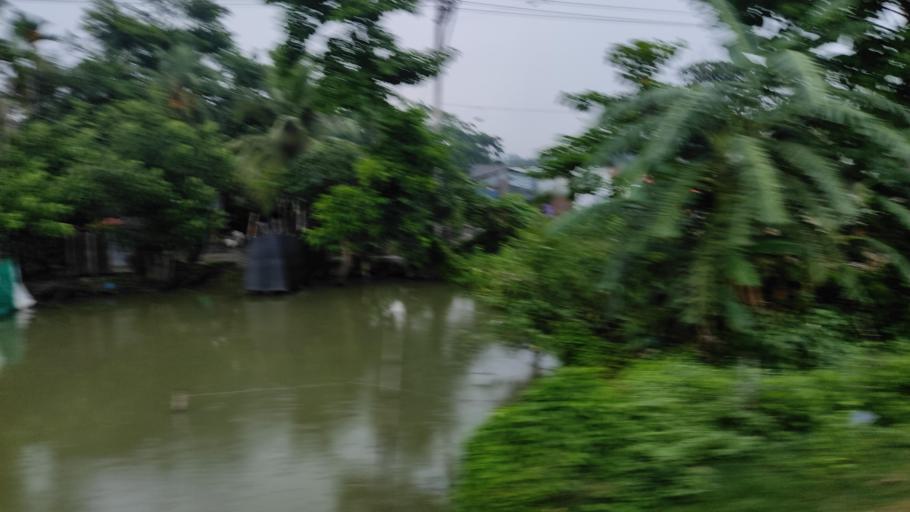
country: BD
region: Barisal
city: Bhandaria
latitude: 22.3166
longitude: 90.3256
